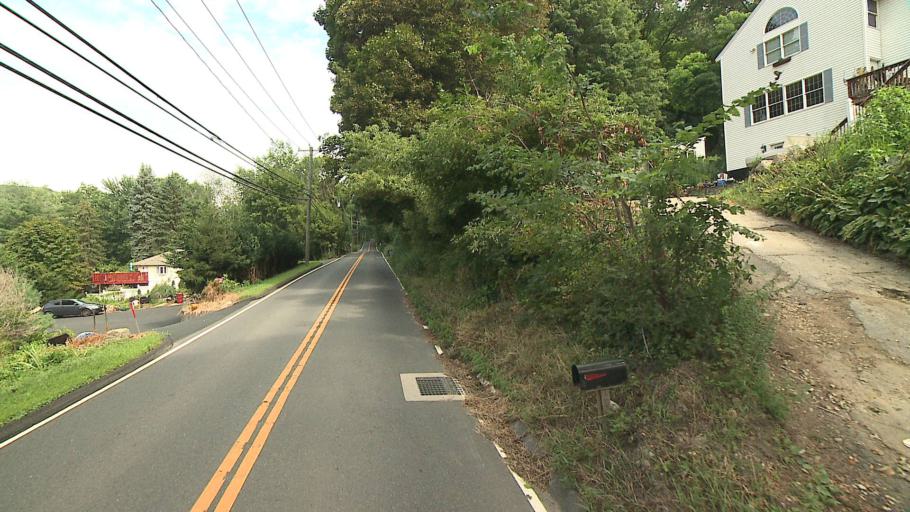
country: US
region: Connecticut
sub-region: Fairfield County
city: Sherman
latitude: 41.5241
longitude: -73.4803
